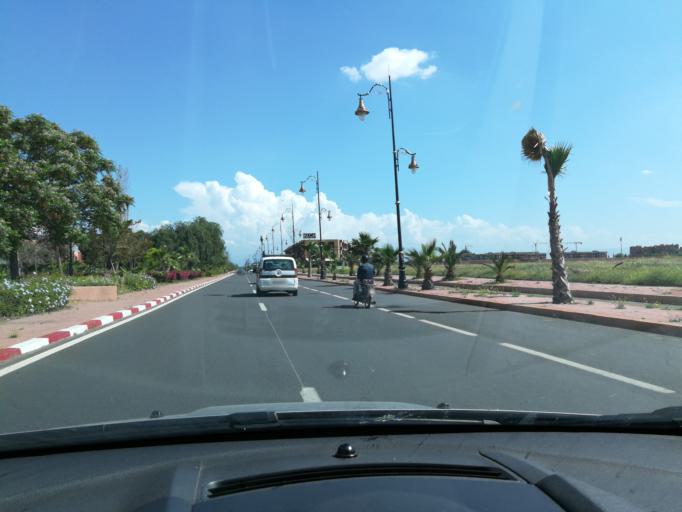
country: MA
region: Marrakech-Tensift-Al Haouz
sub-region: Marrakech
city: Marrakesh
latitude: 31.5894
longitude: -7.9896
